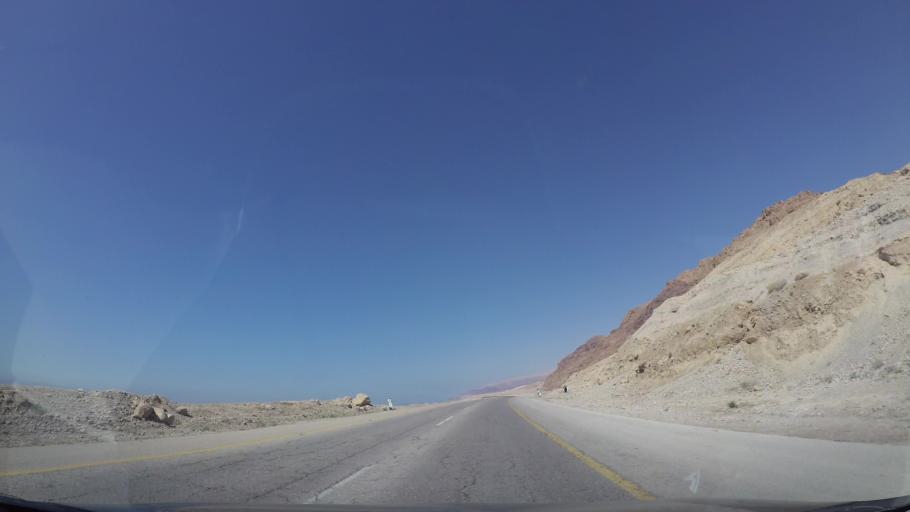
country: JO
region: Karak
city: Al Qasr
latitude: 31.3685
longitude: 35.5468
